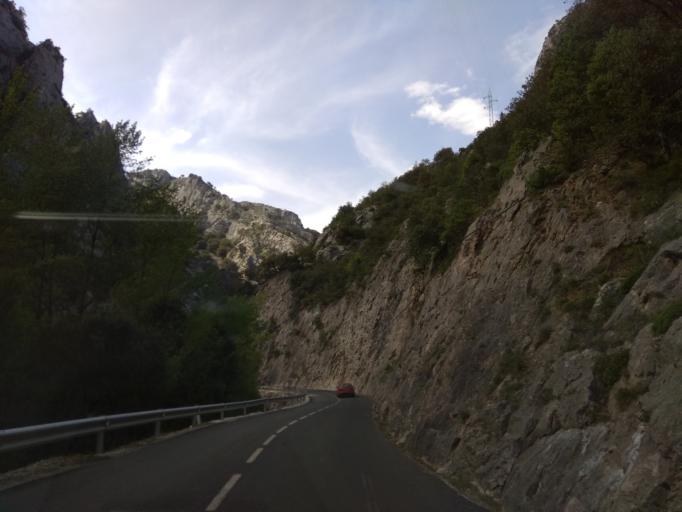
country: ES
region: Cantabria
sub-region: Provincia de Cantabria
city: Potes
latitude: 43.2027
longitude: -4.5914
